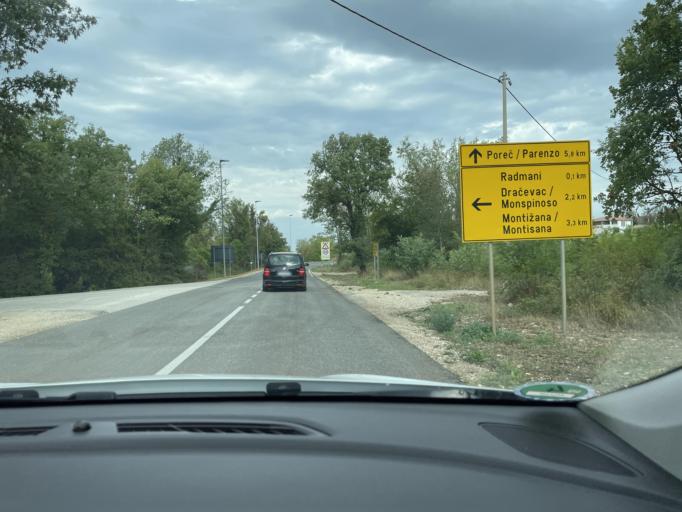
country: HR
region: Istarska
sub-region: Grad Porec
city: Porec
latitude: 45.2063
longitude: 13.6855
